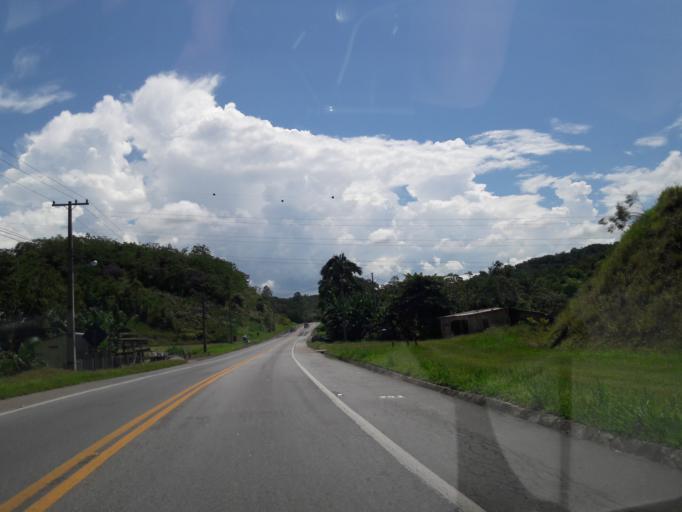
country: BR
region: Parana
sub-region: Antonina
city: Antonina
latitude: -25.5182
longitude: -48.8022
